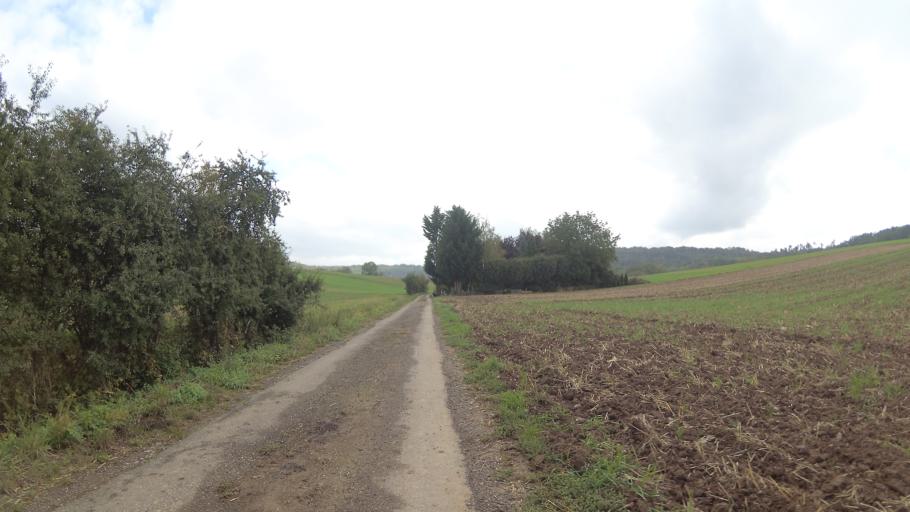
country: DE
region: Baden-Wuerttemberg
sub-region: Regierungsbezirk Stuttgart
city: Erlenbach
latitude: 49.2112
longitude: 9.2868
